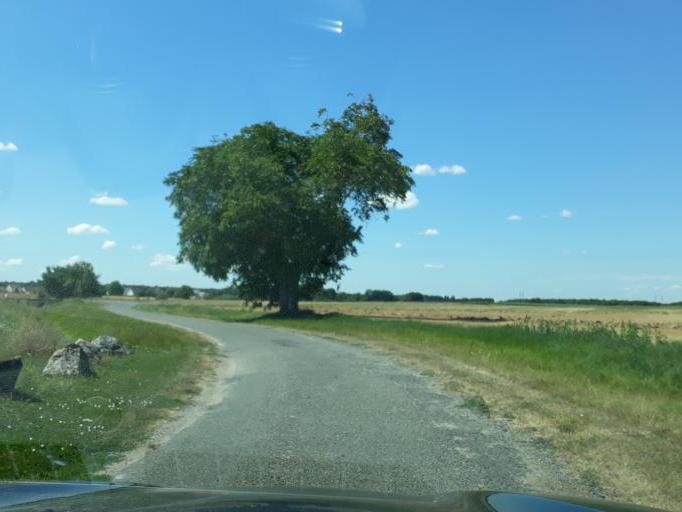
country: FR
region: Centre
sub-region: Departement du Loiret
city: Saran
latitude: 47.9894
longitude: 1.8802
